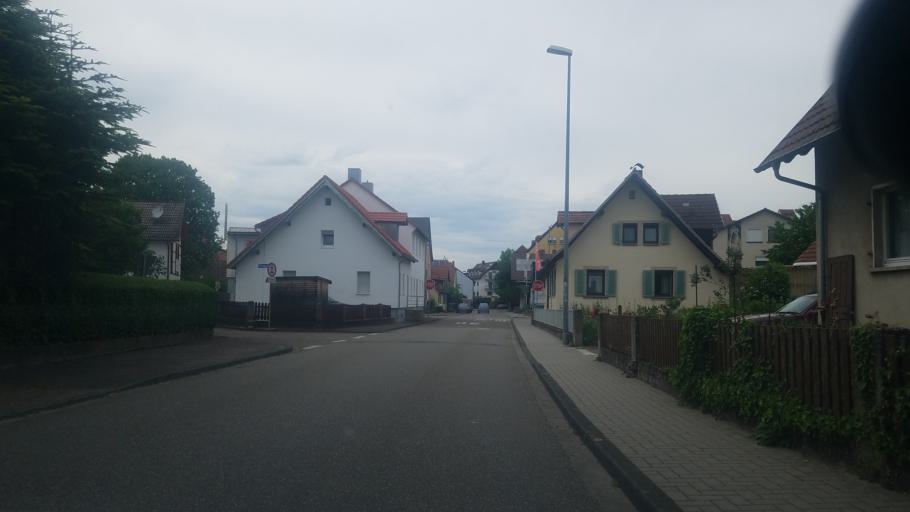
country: DE
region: Baden-Wuerttemberg
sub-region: Freiburg Region
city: Achern
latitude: 48.6263
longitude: 8.0719
